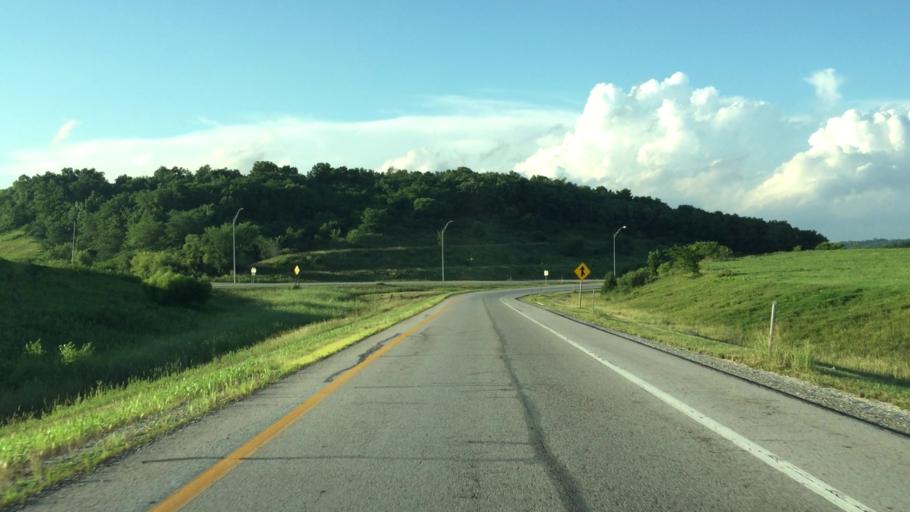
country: US
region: Iowa
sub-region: Johnson County
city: University Heights
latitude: 41.6135
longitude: -91.5493
